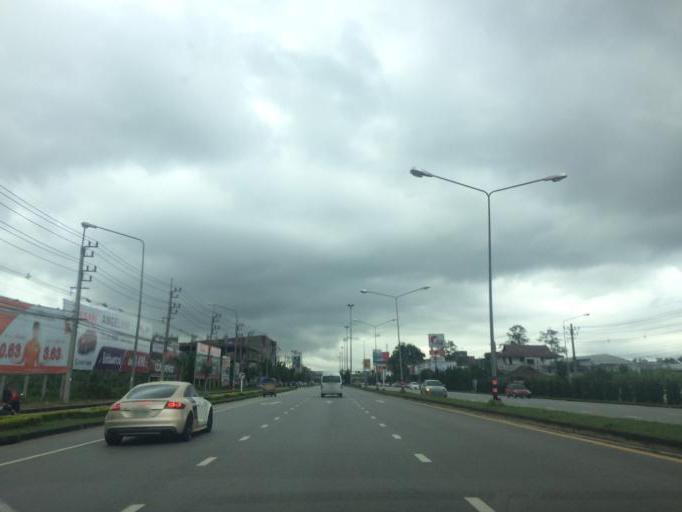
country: TH
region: Chiang Rai
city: Chiang Rai
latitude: 19.8825
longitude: 99.8342
